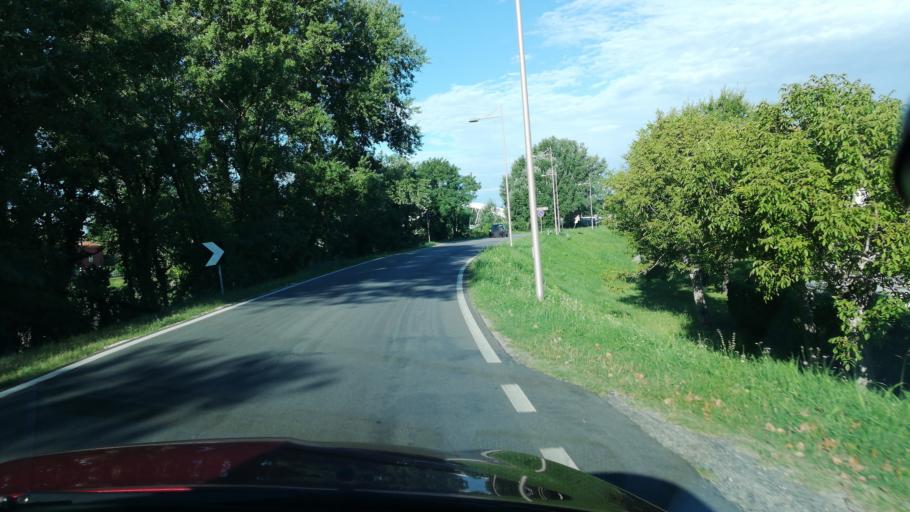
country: IT
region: Veneto
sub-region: Provincia di Venezia
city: Eraclea
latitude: 45.5736
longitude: 12.6770
